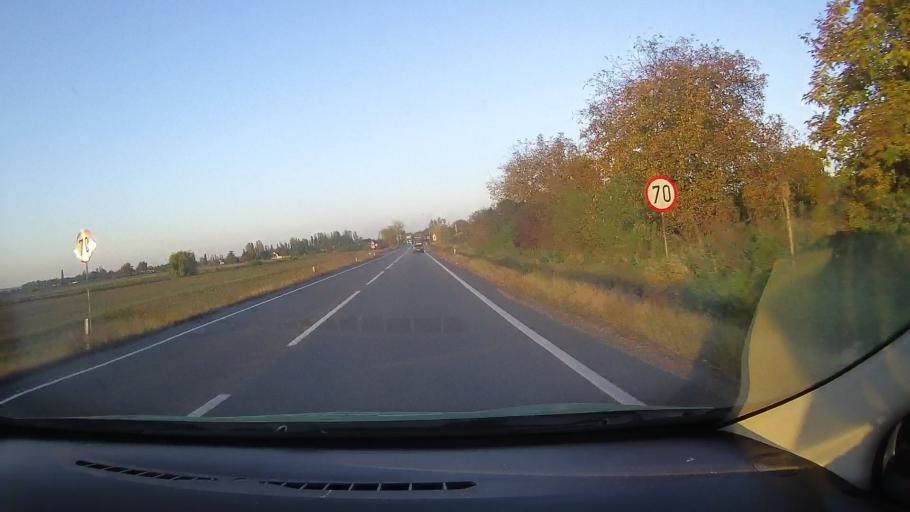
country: RO
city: Dioszeg
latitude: 47.2797
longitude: 21.9848
